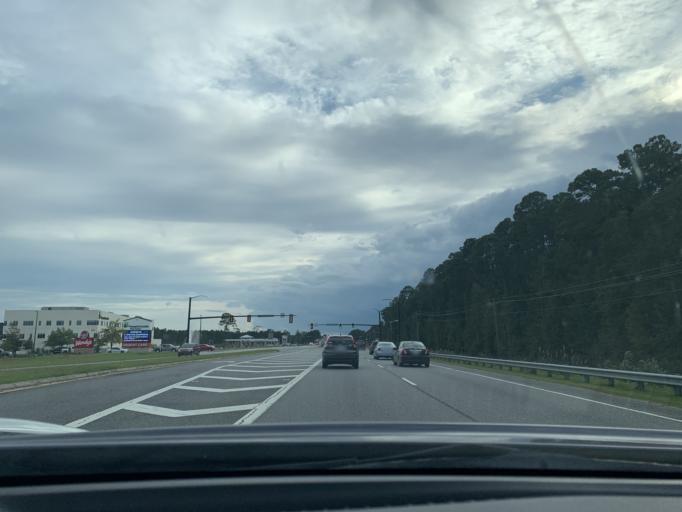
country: US
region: Georgia
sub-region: Chatham County
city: Pooler
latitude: 32.0919
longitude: -81.2754
